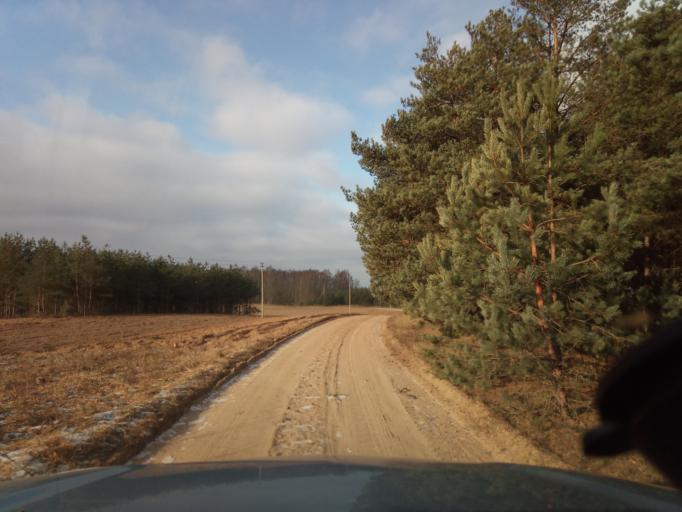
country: LT
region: Alytaus apskritis
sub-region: Alytaus rajonas
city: Daugai
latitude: 54.3764
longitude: 24.4014
